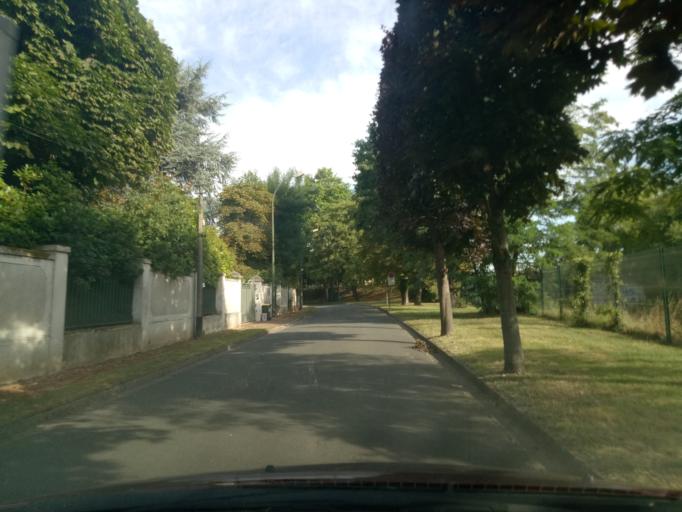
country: FR
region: Ile-de-France
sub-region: Departement des Yvelines
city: Le Vesinet
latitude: 48.8955
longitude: 2.1235
